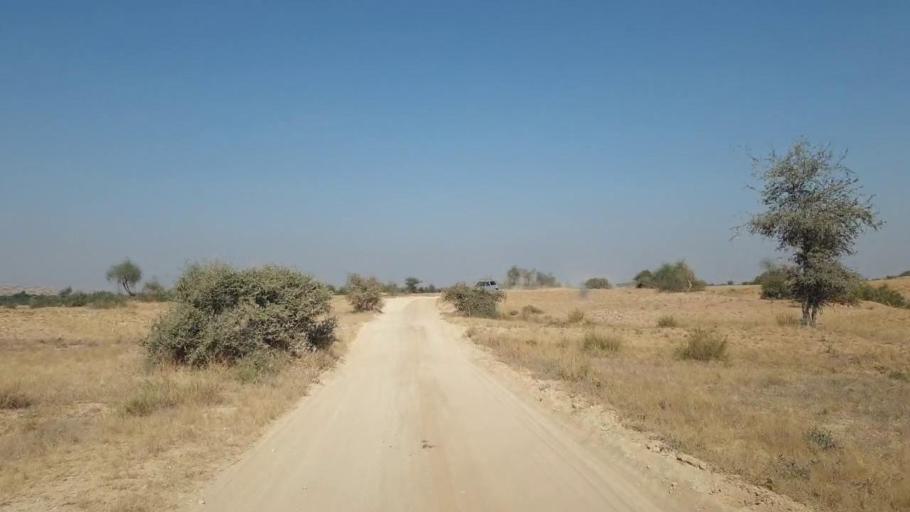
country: PK
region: Sindh
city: Jamshoro
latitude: 25.2785
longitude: 67.8073
